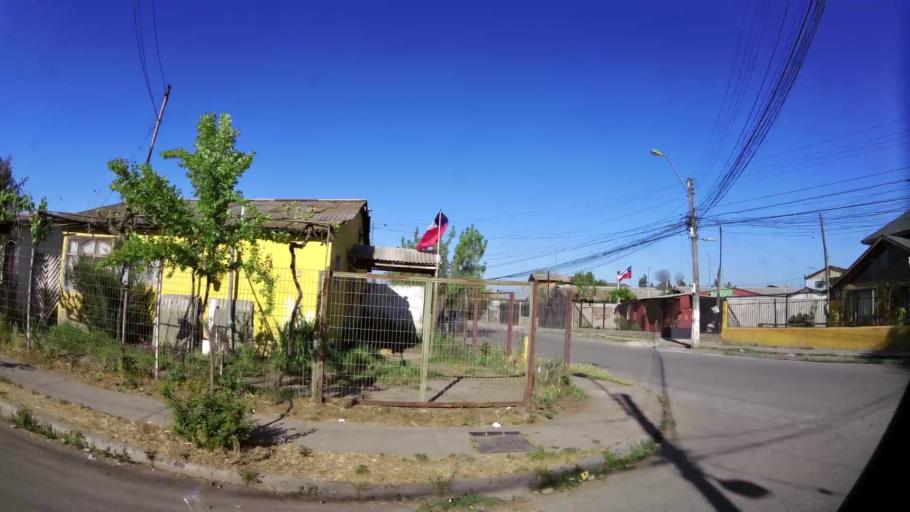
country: CL
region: Santiago Metropolitan
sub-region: Provincia de Talagante
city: Penaflor
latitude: -33.6137
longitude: -70.8729
